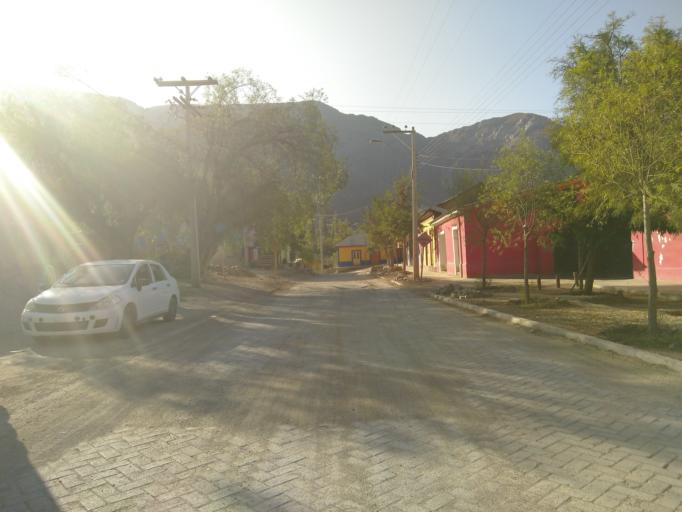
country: CL
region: Coquimbo
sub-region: Provincia de Limari
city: Monte Patria
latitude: -30.9645
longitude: -70.7691
